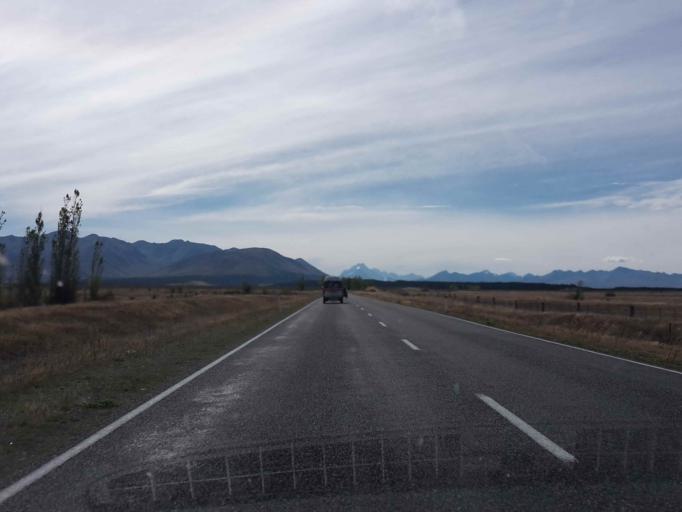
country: NZ
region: Canterbury
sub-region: Timaru District
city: Pleasant Point
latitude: -44.2279
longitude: 170.1164
